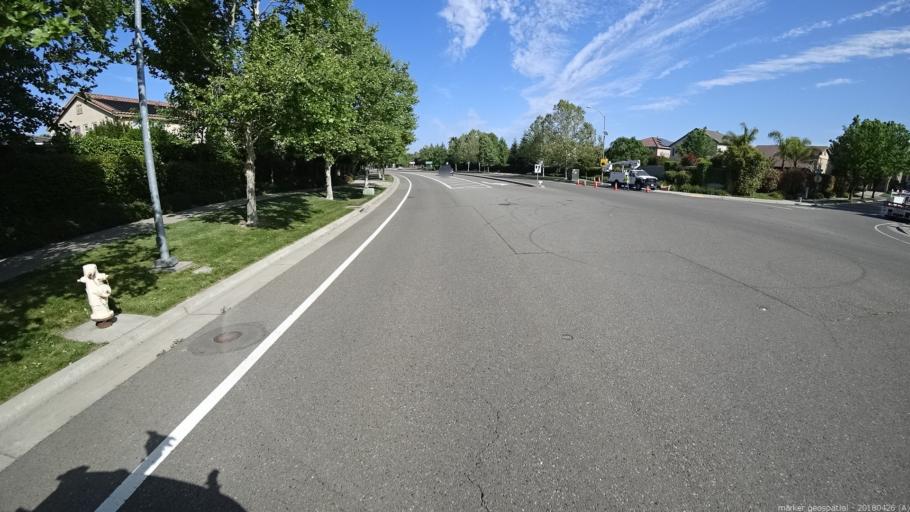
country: US
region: California
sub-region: Yolo County
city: West Sacramento
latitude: 38.5514
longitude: -121.5192
